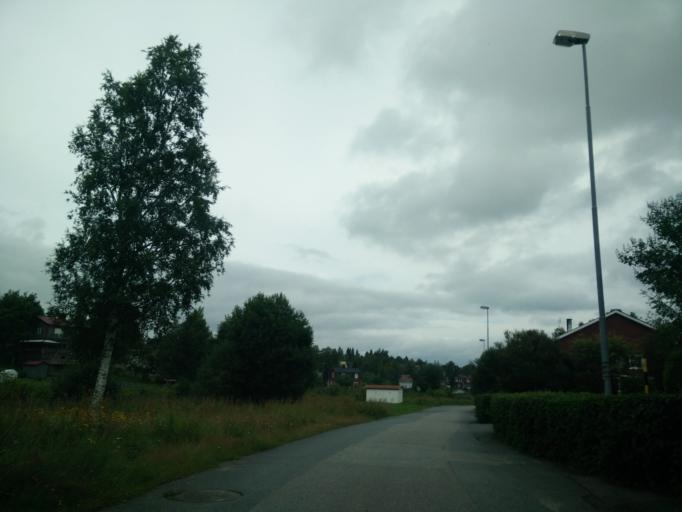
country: SE
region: Vaesternorrland
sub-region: Haernoesands Kommun
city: Haernoesand
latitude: 62.6289
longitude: 17.9176
